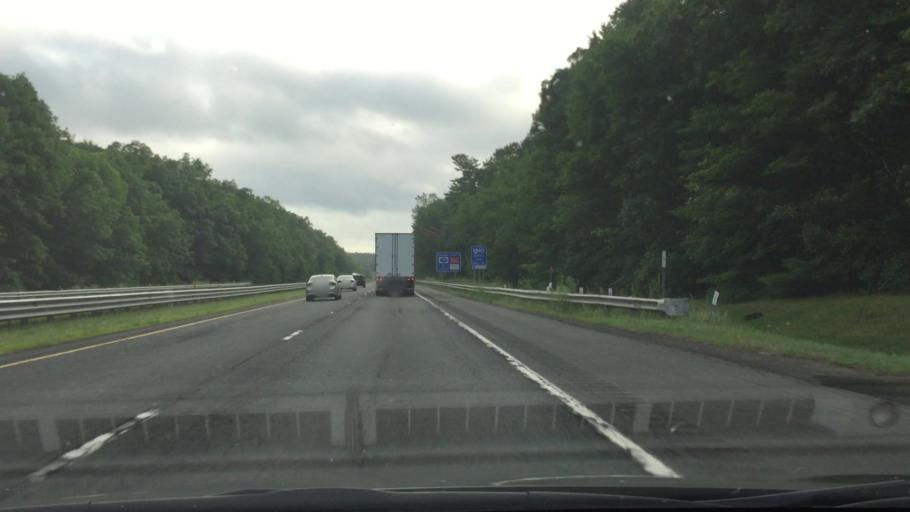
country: US
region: Massachusetts
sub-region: Hampden County
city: Westfield
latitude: 42.1420
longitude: -72.6822
